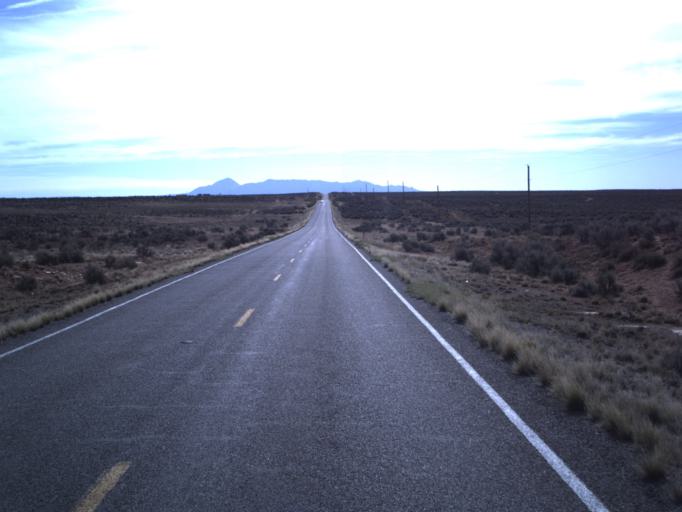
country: US
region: Utah
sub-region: San Juan County
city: Blanding
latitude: 37.4282
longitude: -109.3559
